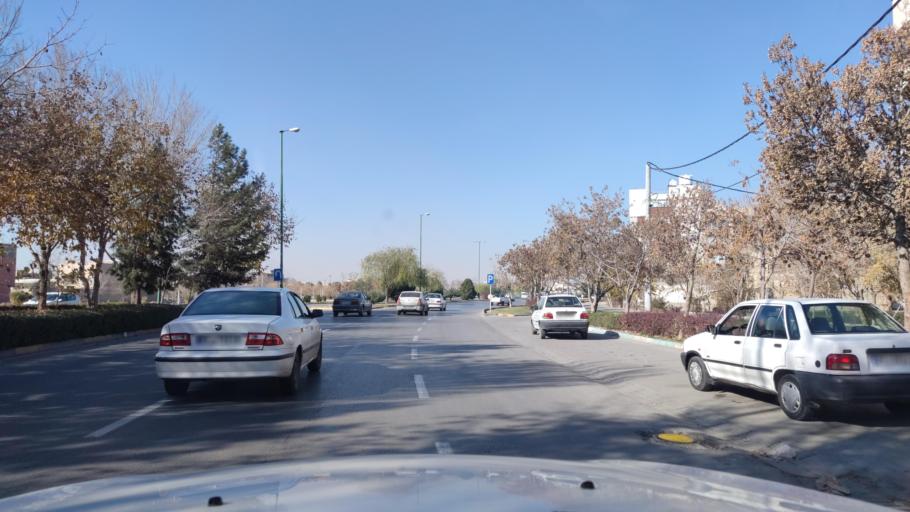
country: IR
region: Isfahan
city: Isfahan
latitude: 32.6810
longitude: 51.6480
